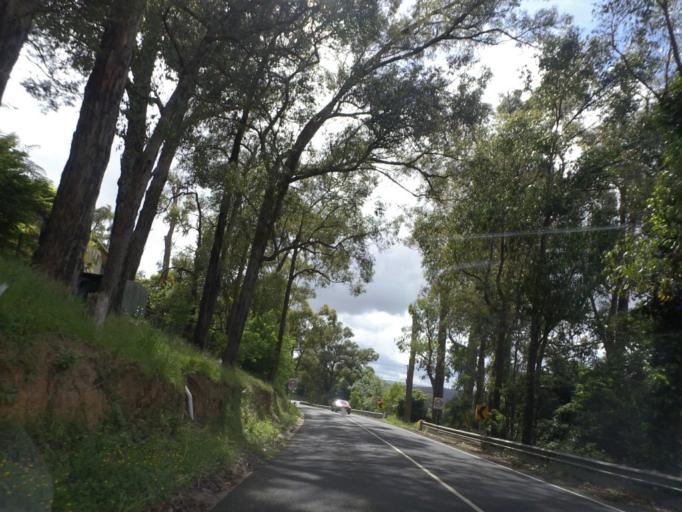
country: AU
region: Victoria
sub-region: Cardinia
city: Cockatoo
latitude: -37.9251
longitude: 145.4749
